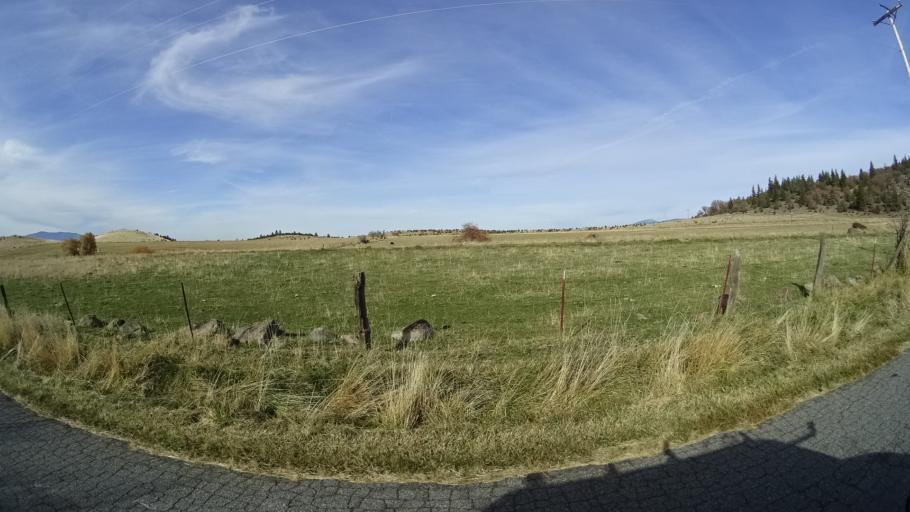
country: US
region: California
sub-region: Siskiyou County
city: Weed
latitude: 41.4651
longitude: -122.3906
